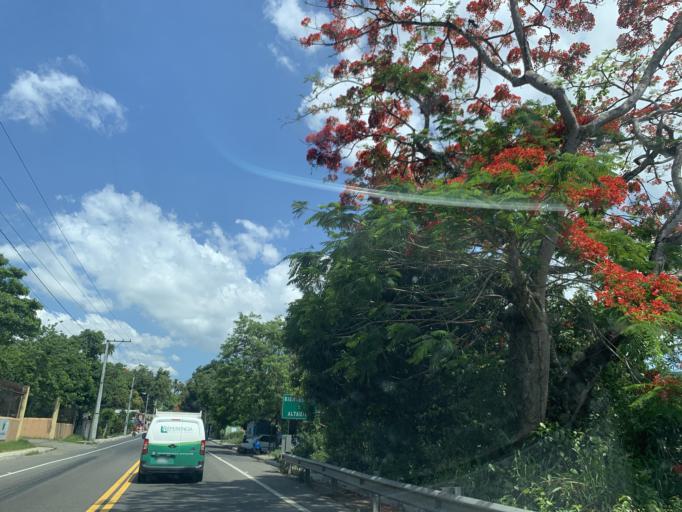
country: DO
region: Puerto Plata
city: Altamira
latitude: 19.6840
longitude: -70.8401
